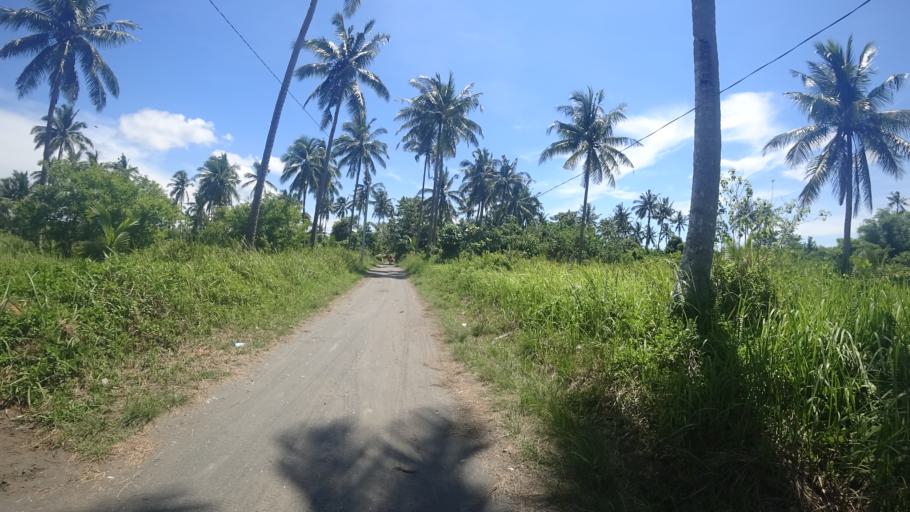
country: PH
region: Eastern Visayas
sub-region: Province of Leyte
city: Mayorga
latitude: 10.8958
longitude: 125.0124
